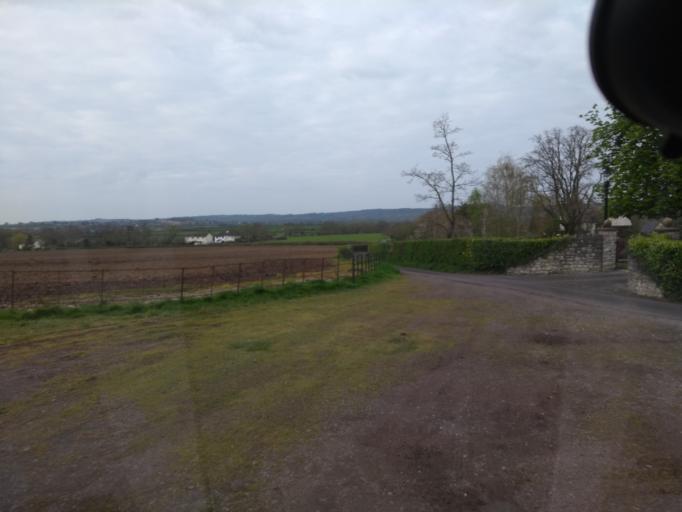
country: GB
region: England
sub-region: Somerset
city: Ilminster
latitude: 50.9787
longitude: -2.9619
